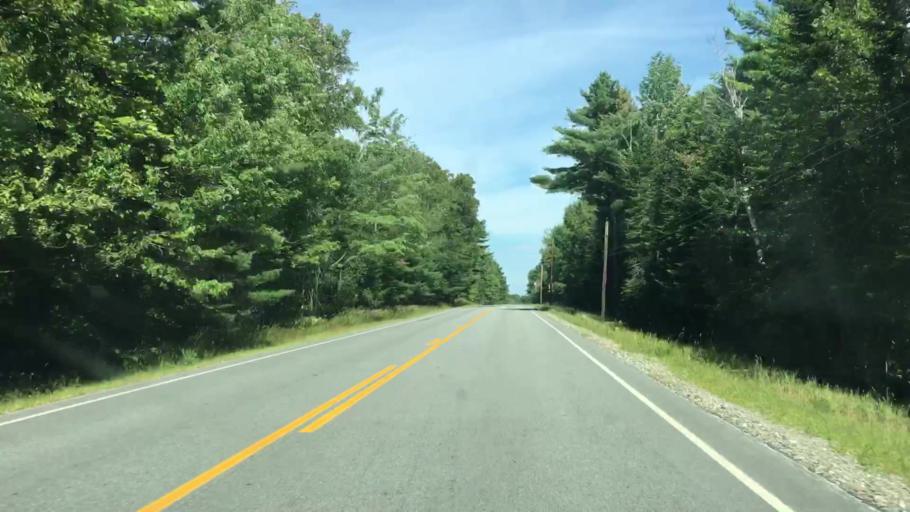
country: US
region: Maine
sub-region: Penobscot County
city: Howland
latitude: 45.2190
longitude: -68.7889
